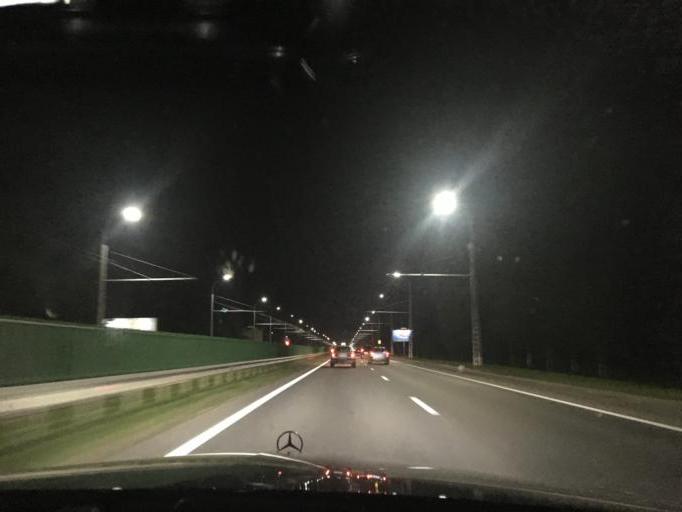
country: BY
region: Brest
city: Brest
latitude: 52.1061
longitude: 23.7968
